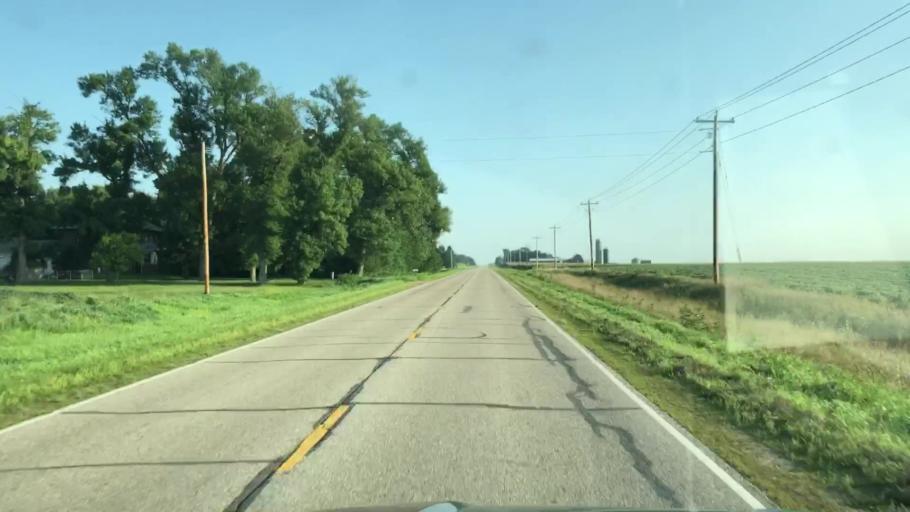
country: US
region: Iowa
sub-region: Lyon County
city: George
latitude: 43.3650
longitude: -95.9983
